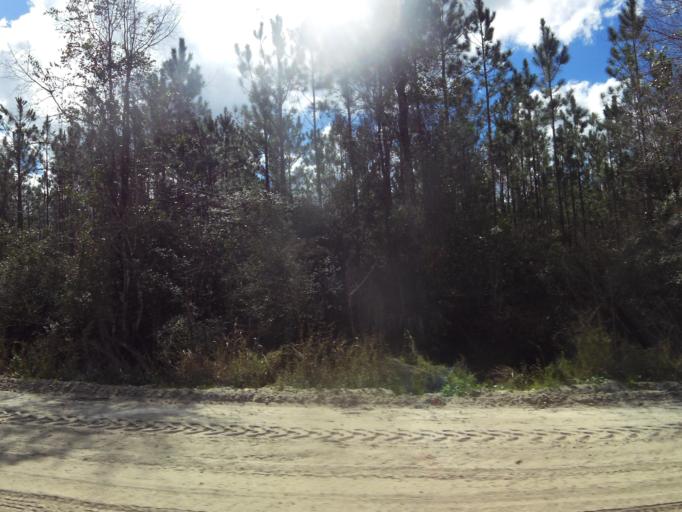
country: US
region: Florida
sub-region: Clay County
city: Green Cove Springs
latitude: 29.8367
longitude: -81.7798
